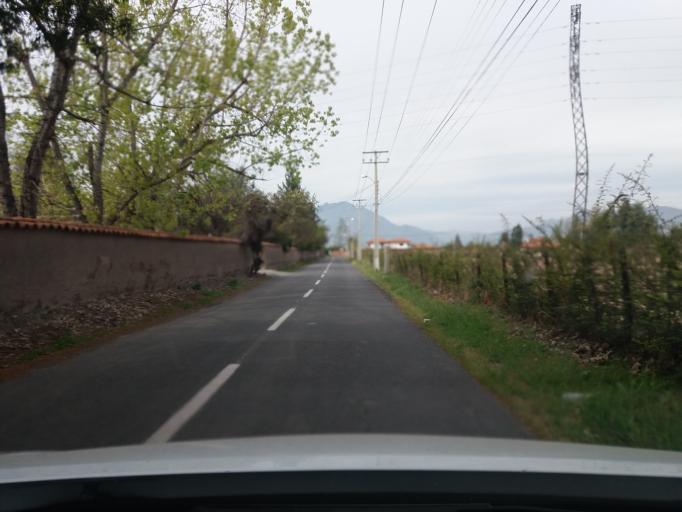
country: CL
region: Valparaiso
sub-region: Provincia de Los Andes
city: Los Andes
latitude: -32.8275
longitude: -70.6585
